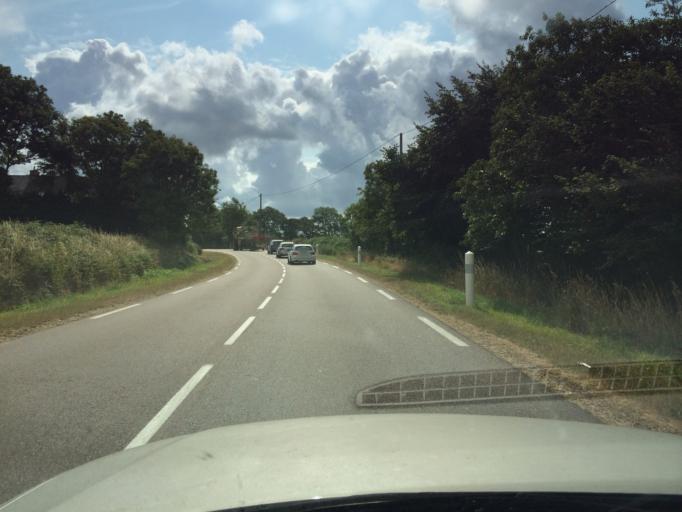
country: FR
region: Lower Normandy
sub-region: Departement de la Manche
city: Martinvast
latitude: 49.5592
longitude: -1.6617
